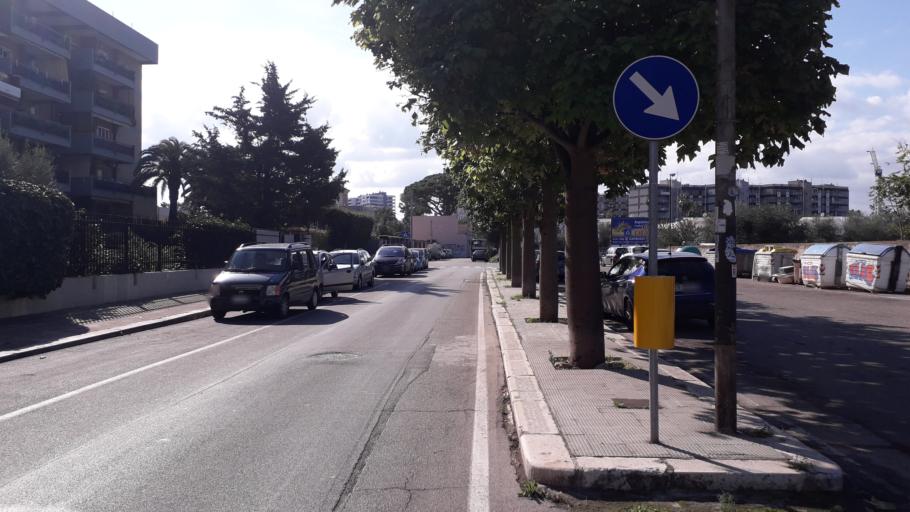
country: IT
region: Apulia
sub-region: Provincia di Bari
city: Bari
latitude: 41.1123
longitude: 16.8555
